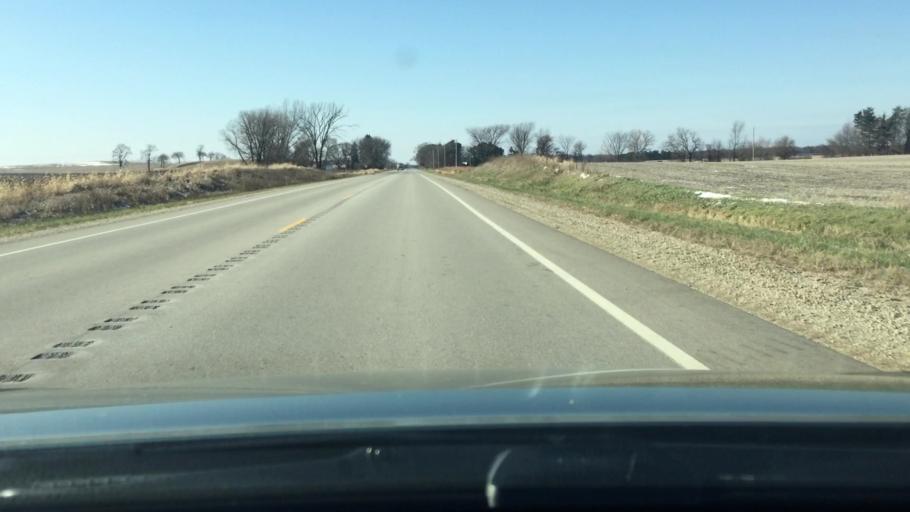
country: US
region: Wisconsin
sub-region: Jefferson County
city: Lake Ripley
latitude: 43.0077
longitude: -88.9171
